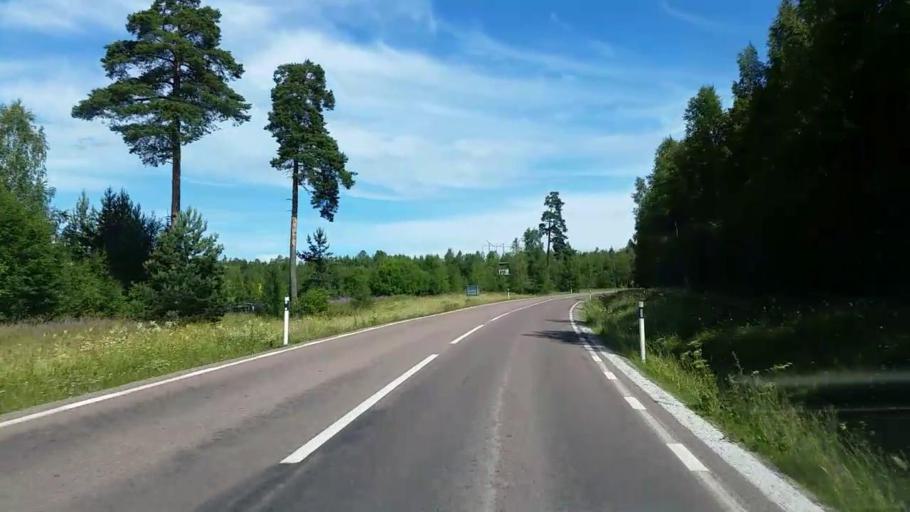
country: SE
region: Dalarna
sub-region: Rattviks Kommun
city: Raettvik
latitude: 60.8960
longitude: 15.1496
